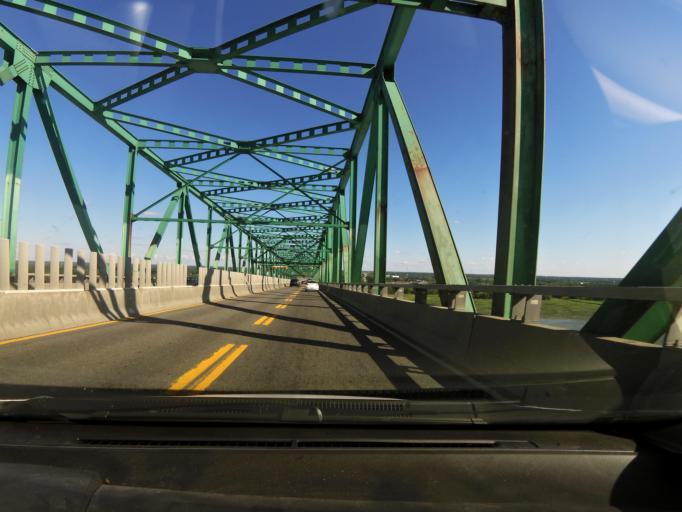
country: CA
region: Quebec
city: Sainte-Catherine
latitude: 46.3058
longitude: -72.5585
